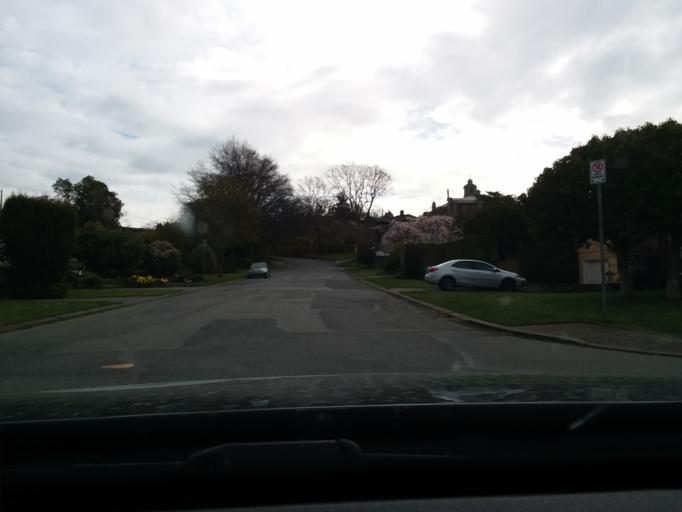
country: CA
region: British Columbia
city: Oak Bay
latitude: 48.4481
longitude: -123.3283
